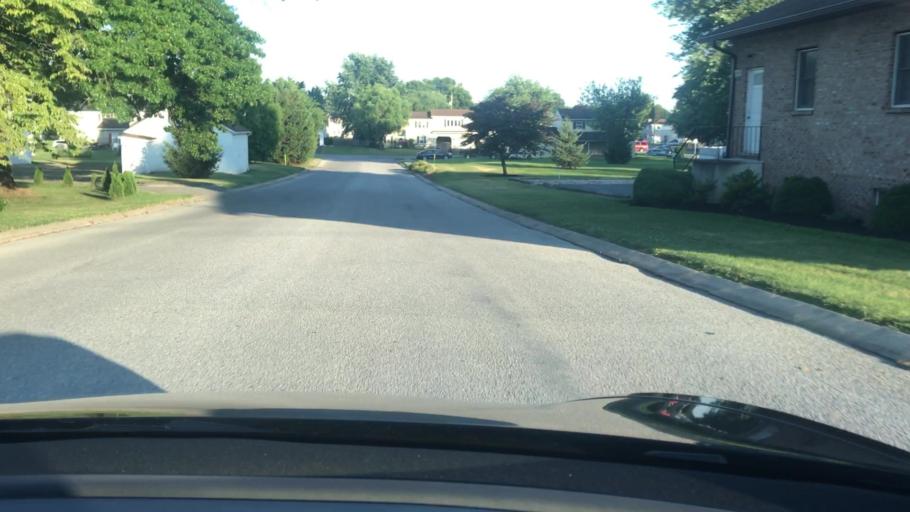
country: US
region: Pennsylvania
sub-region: York County
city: Shiloh
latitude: 39.9738
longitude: -76.7950
